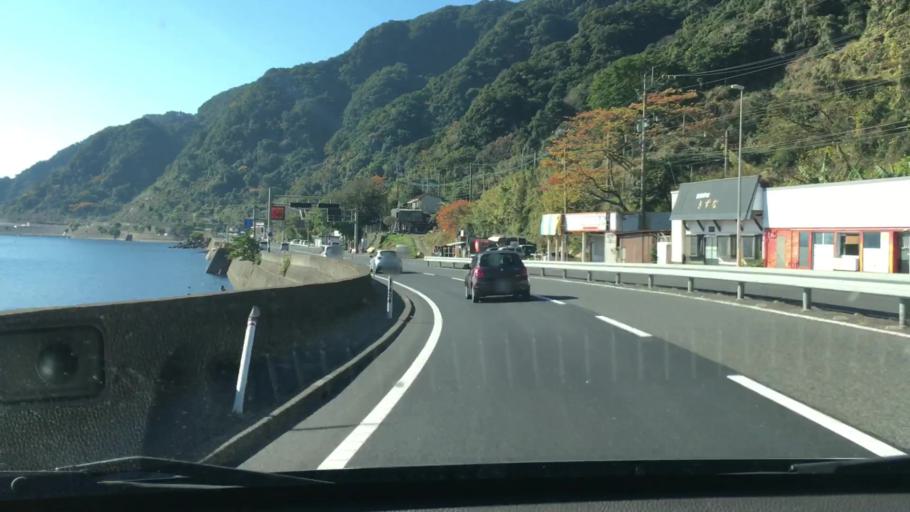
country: JP
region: Kagoshima
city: Kagoshima-shi
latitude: 31.6502
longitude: 130.6063
